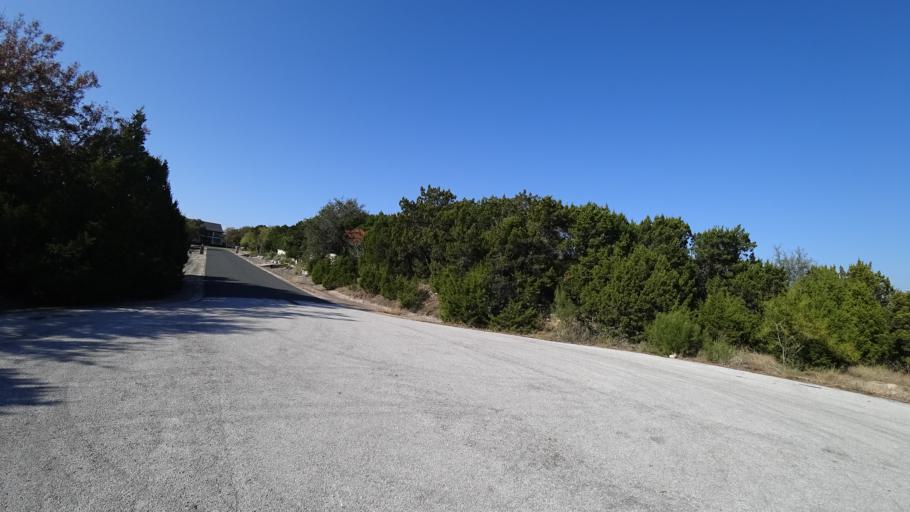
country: US
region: Texas
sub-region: Williamson County
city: Anderson Mill
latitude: 30.3819
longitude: -97.8255
